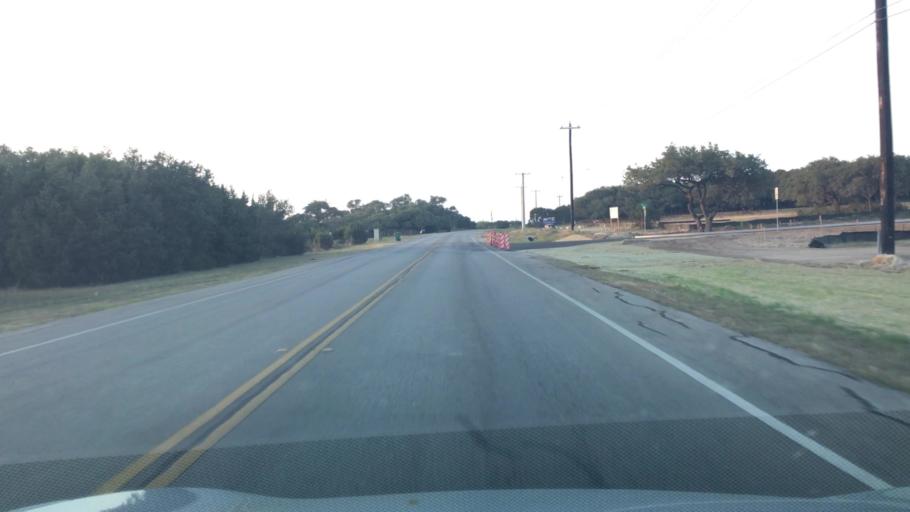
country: US
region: Texas
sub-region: Hays County
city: Dripping Springs
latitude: 30.1641
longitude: -98.0085
